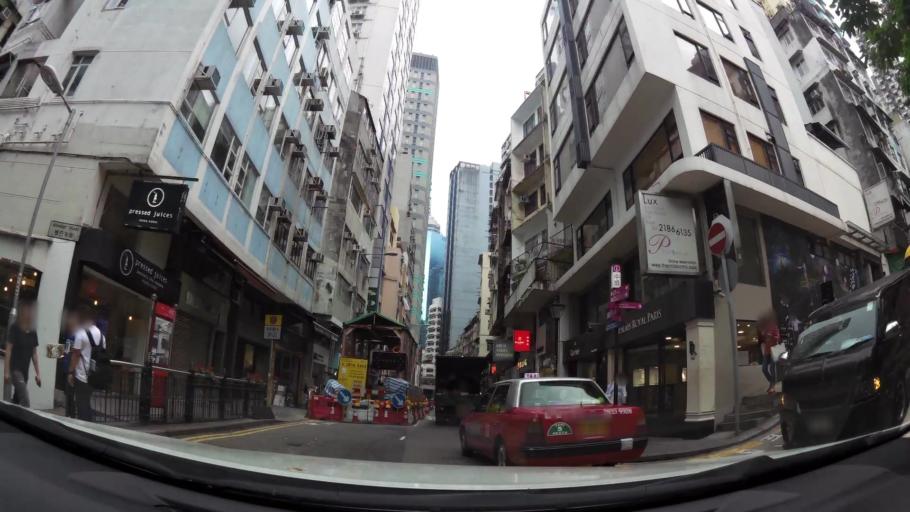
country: HK
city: Hong Kong
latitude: 22.2838
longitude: 114.1521
